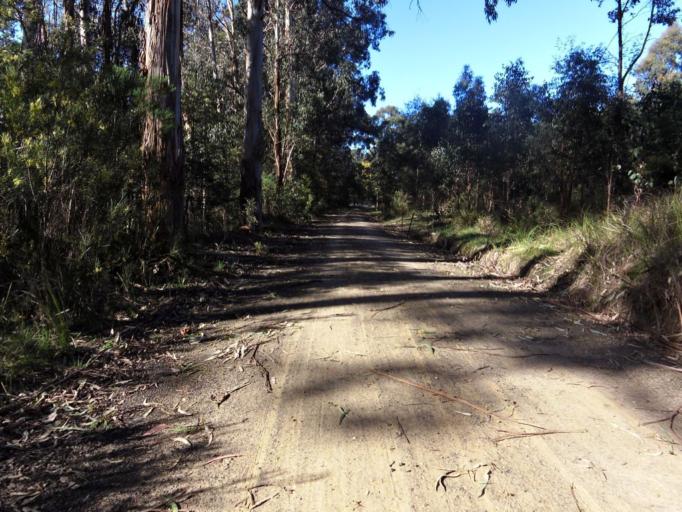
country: AU
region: Victoria
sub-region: Latrobe
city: Moe
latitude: -38.3710
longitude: 146.2040
